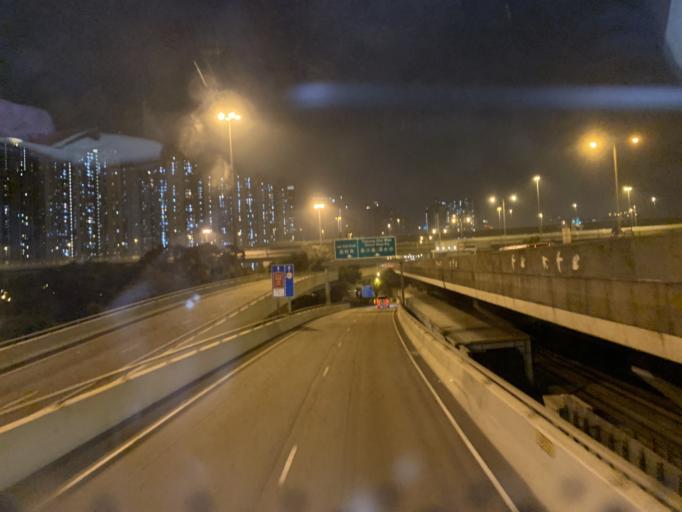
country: HK
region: Sham Shui Po
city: Sham Shui Po
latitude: 22.3326
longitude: 114.1410
